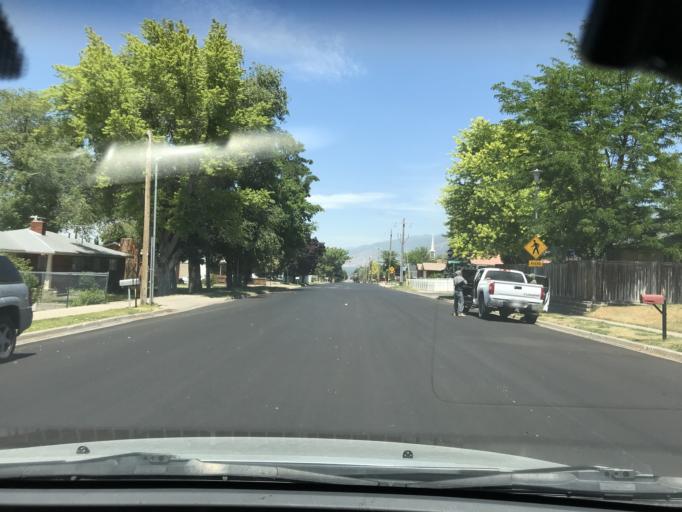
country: US
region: Utah
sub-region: Davis County
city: Woods Cross
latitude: 40.8632
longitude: -111.8858
